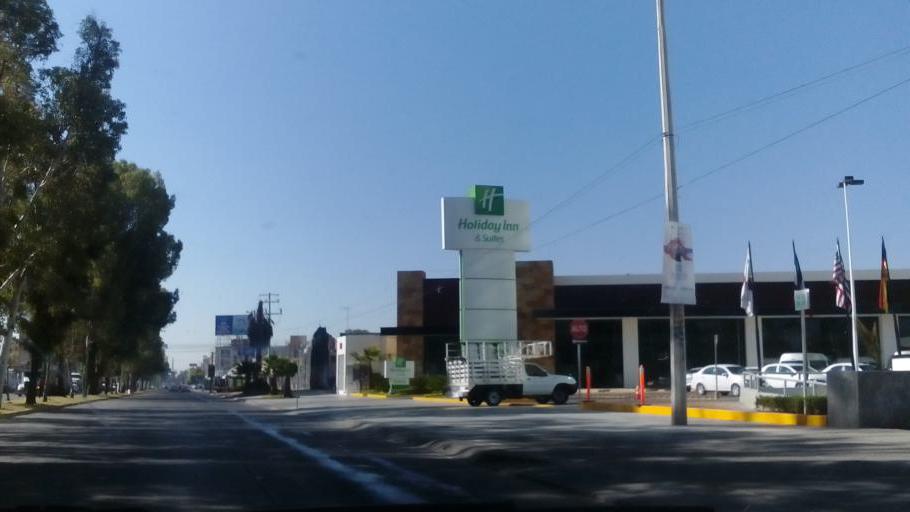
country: MX
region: Guanajuato
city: Leon
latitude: 21.1532
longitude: -101.6845
